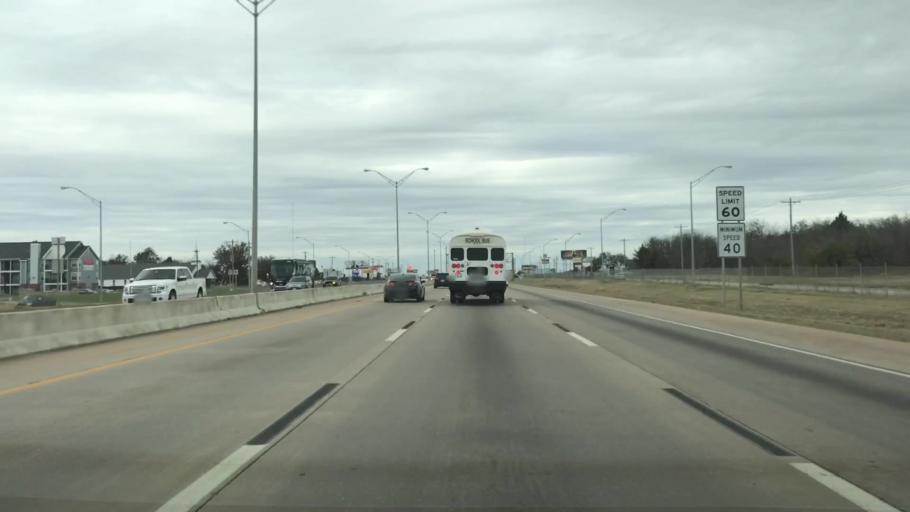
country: US
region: Oklahoma
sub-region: Cleveland County
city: Moore
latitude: 35.3707
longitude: -97.4948
